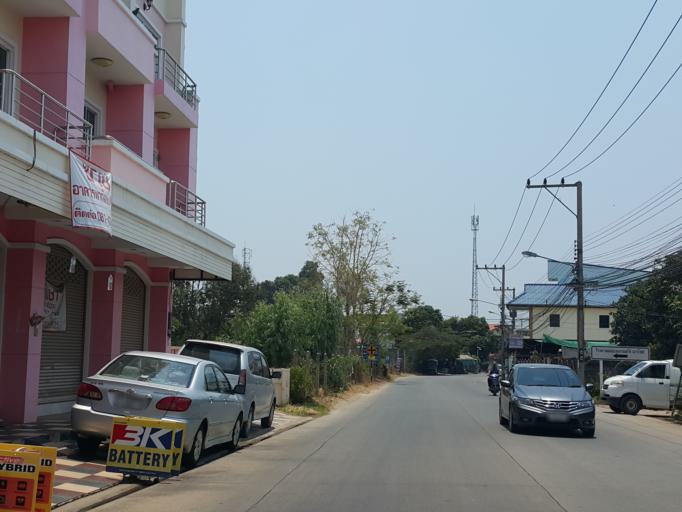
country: TH
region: Phitsanulok
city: Phitsanulok
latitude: 16.8106
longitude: 100.2462
